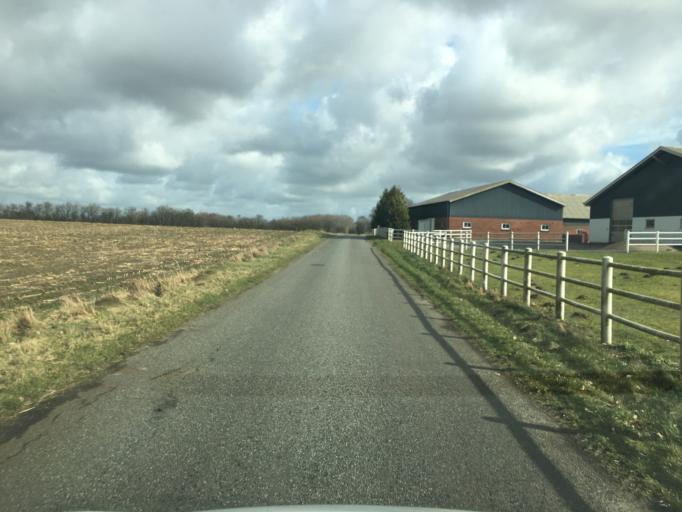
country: DK
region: South Denmark
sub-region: Aabenraa Kommune
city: Krusa
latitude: 54.9150
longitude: 9.3437
